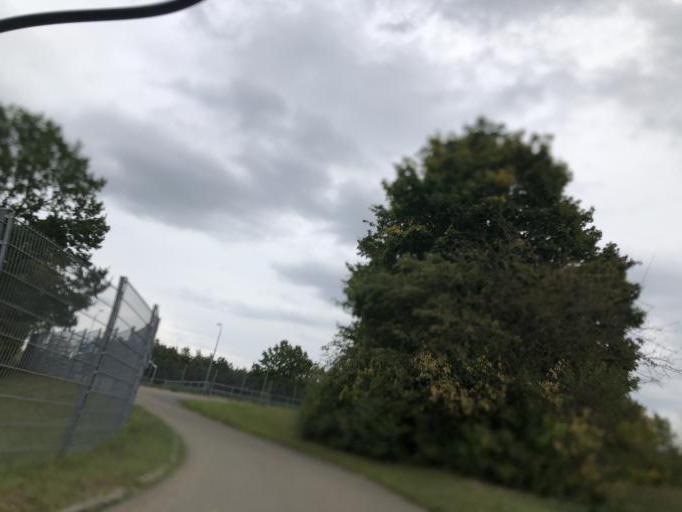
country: DE
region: Bavaria
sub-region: Regierungsbezirk Mittelfranken
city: Erlangen
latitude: 49.5546
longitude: 10.9688
